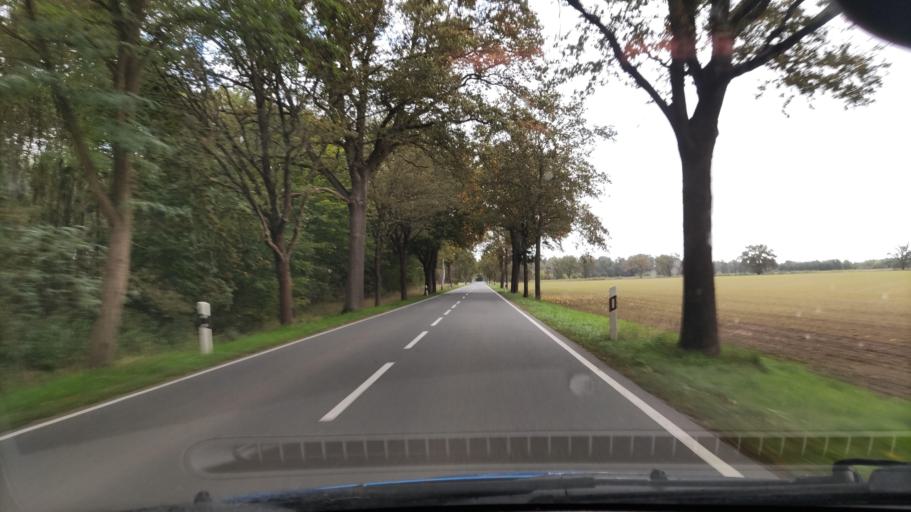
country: DE
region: Brandenburg
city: Lanz
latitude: 53.0054
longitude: 11.5499
